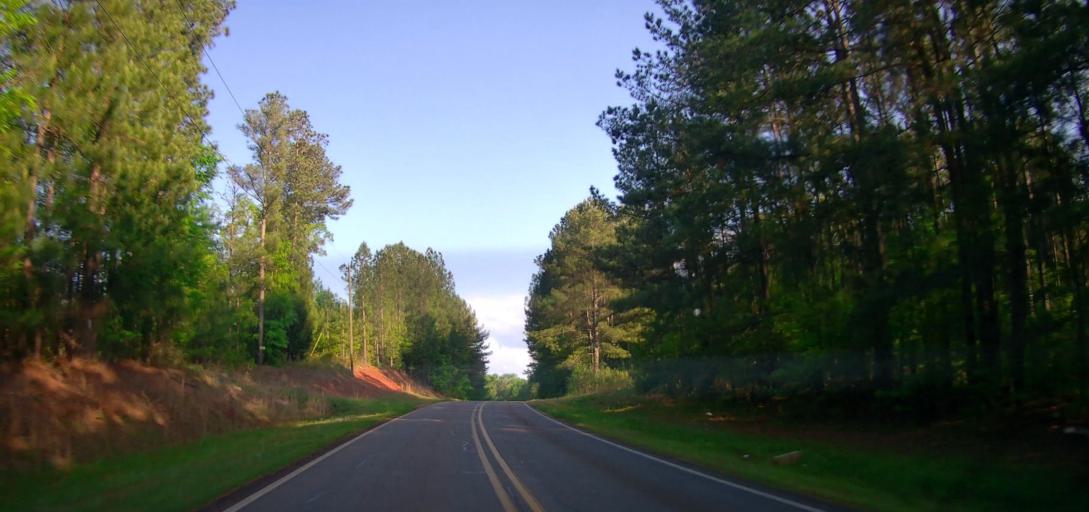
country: US
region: Georgia
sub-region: Putnam County
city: Eatonton
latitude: 33.2877
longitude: -83.3262
